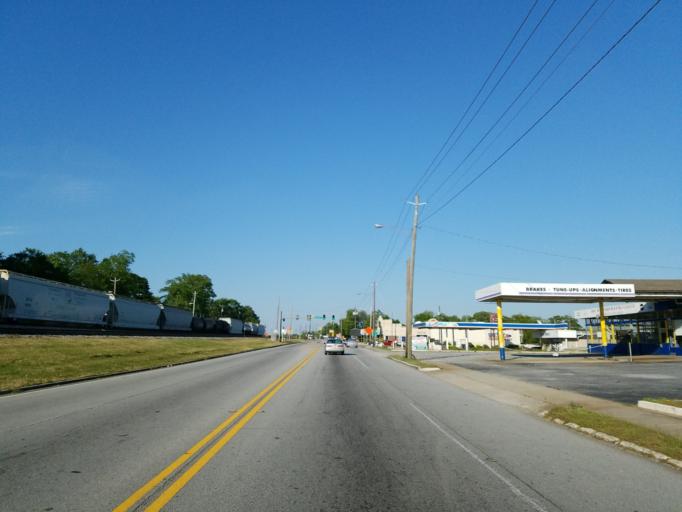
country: US
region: Georgia
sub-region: Douglas County
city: Douglasville
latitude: 33.7534
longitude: -84.7432
